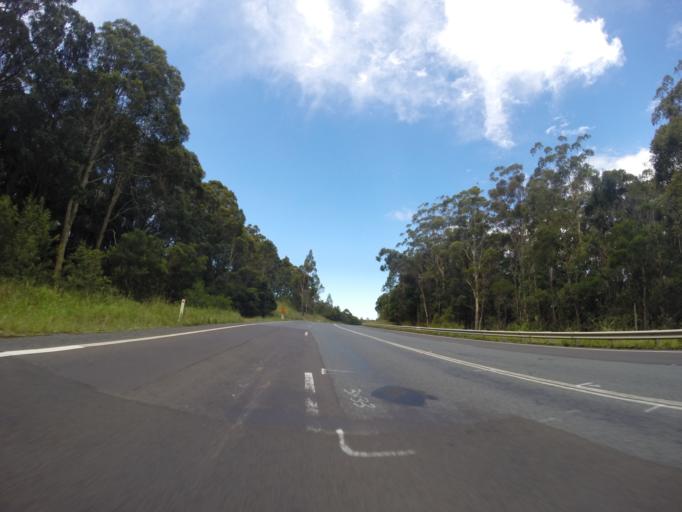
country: AU
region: New South Wales
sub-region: Shoalhaven Shire
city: Falls Creek
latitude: -35.0758
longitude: 150.5591
